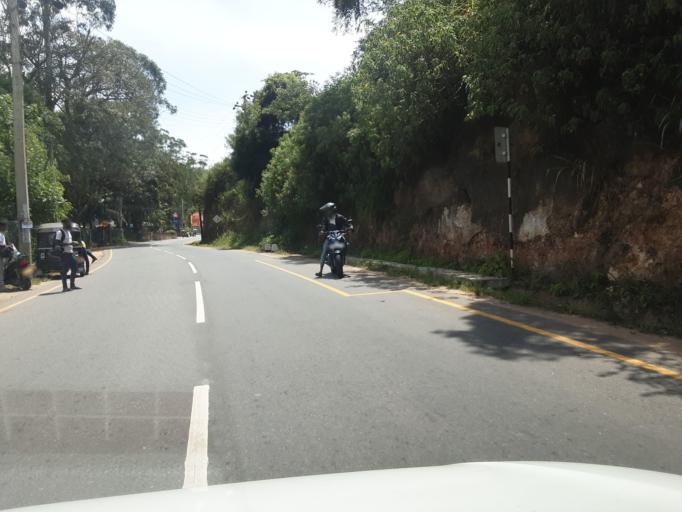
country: LK
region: Central
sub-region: Nuwara Eliya District
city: Nuwara Eliya
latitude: 6.9094
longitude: 80.9059
